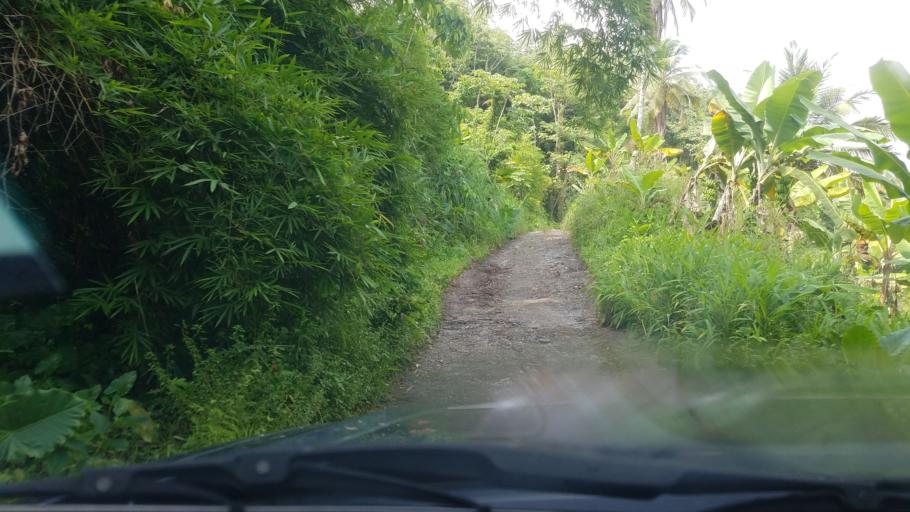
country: LC
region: Anse-la-Raye
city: Anse La Raye
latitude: 13.9401
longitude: -60.9901
